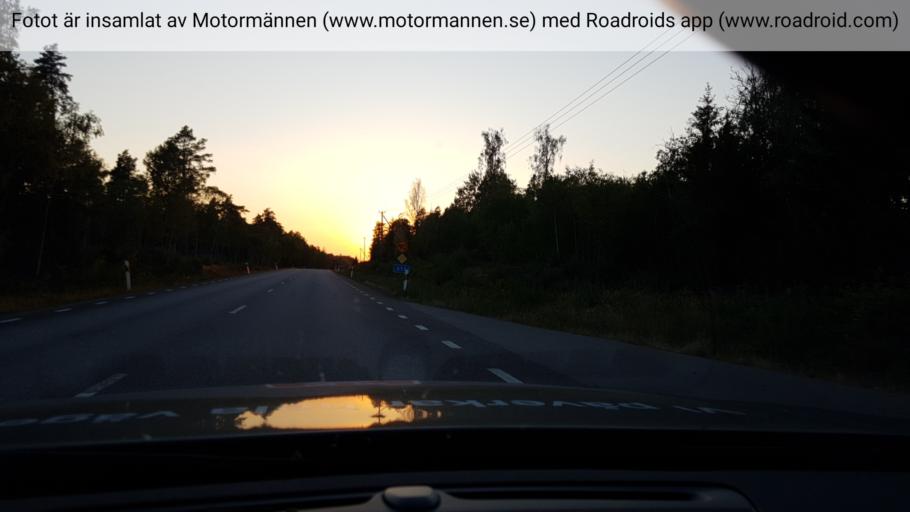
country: SE
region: Uppsala
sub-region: Osthammars Kommun
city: Bjorklinge
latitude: 59.9701
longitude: 17.3708
